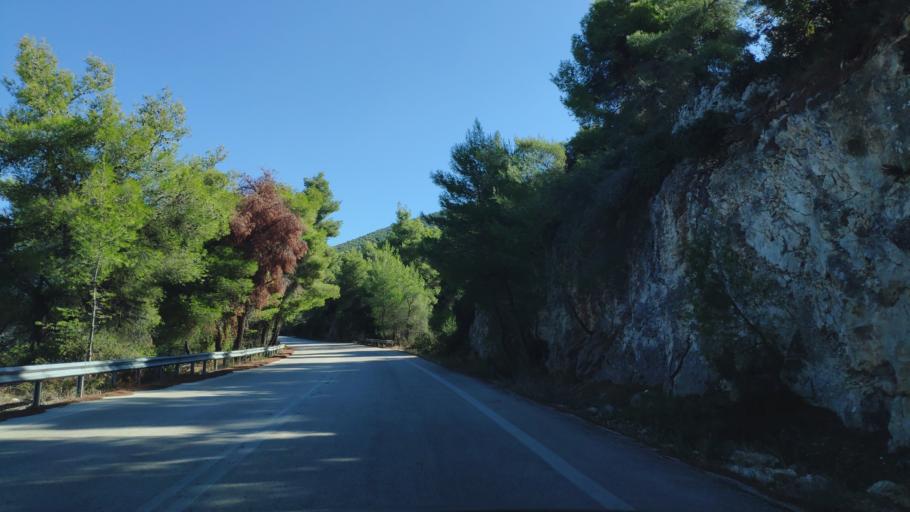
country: GR
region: Peloponnese
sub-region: Nomos Korinthias
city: Sofikon
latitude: 37.8277
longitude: 23.0578
